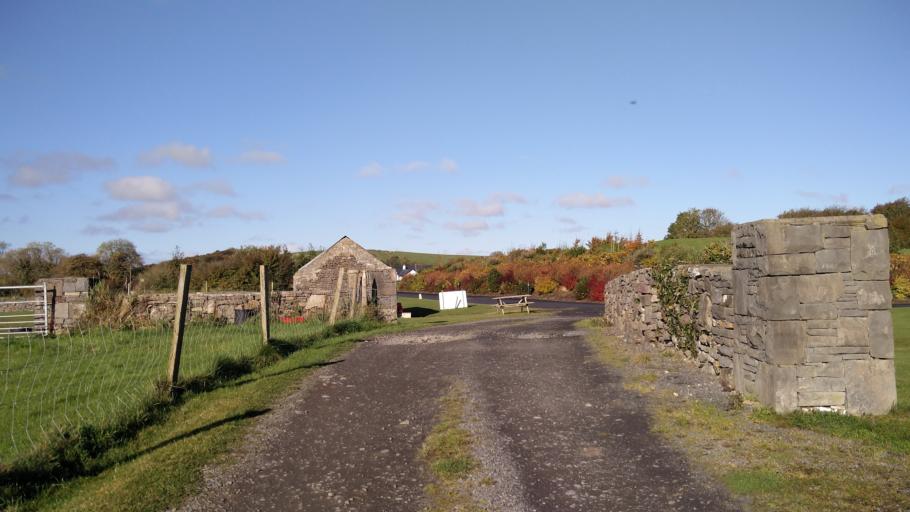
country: IE
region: Connaught
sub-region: Maigh Eo
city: Westport
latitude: 53.7839
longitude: -9.4640
